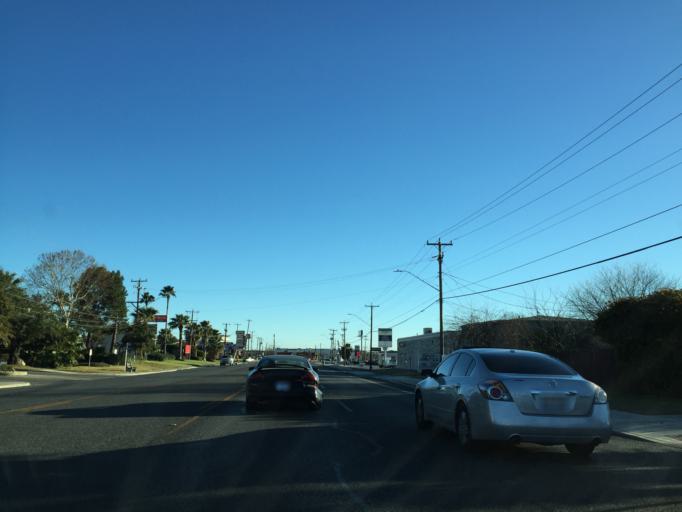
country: US
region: Texas
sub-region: Bexar County
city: Castle Hills
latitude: 29.5258
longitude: -98.5052
